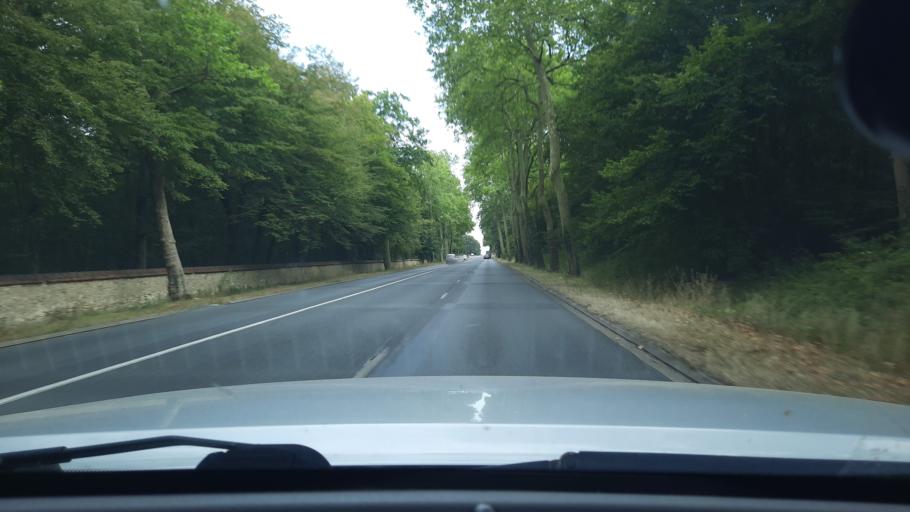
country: FR
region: Ile-de-France
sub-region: Departement de Seine-et-Marne
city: La Rochette
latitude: 48.5110
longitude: 2.6572
